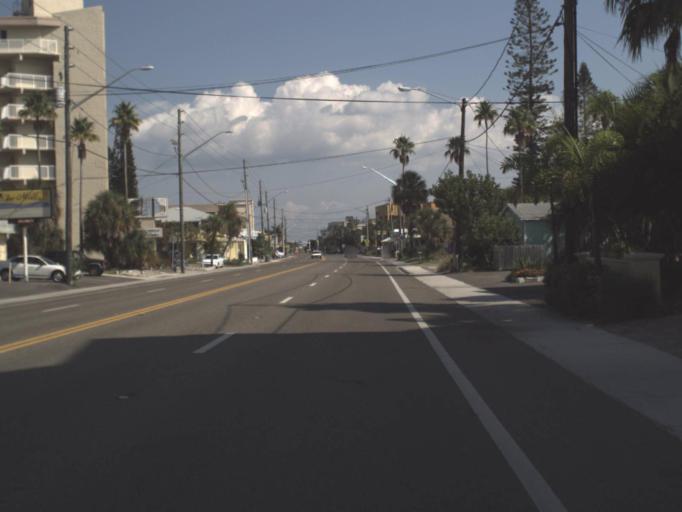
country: US
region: Florida
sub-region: Pinellas County
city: Treasure Island
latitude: 27.7619
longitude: -82.7663
